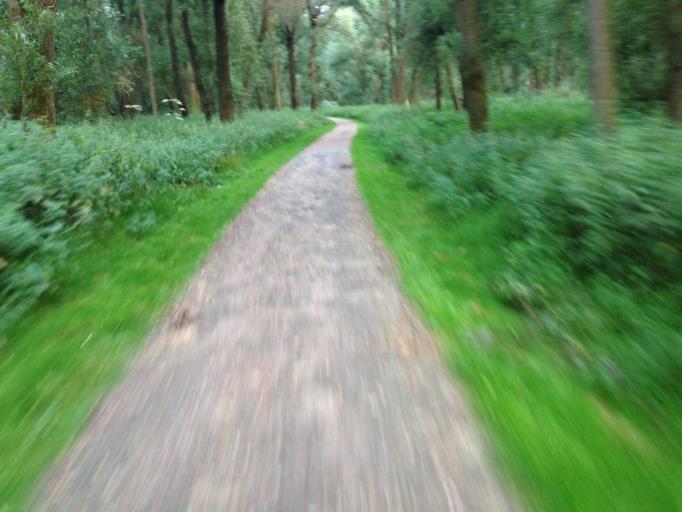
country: NL
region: Flevoland
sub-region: Gemeente Almere
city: Almere Stad
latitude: 52.4111
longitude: 5.2297
